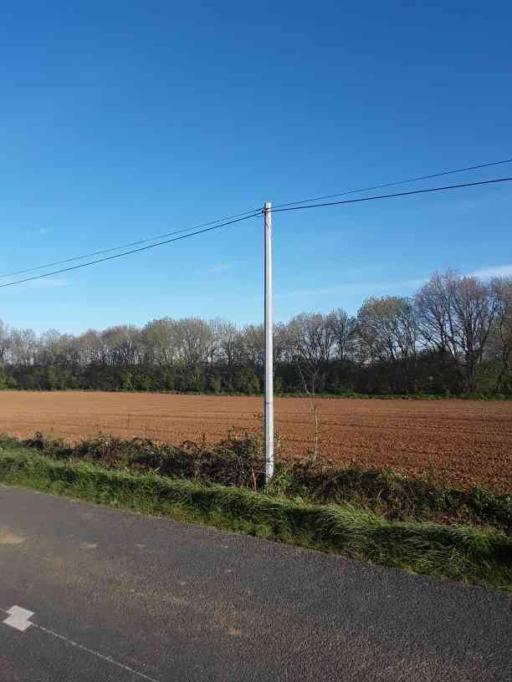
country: FR
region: Pays de la Loire
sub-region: Departement de la Vendee
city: Mareuil-sur-Lay-Dissais
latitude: 46.5397
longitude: -1.1604
